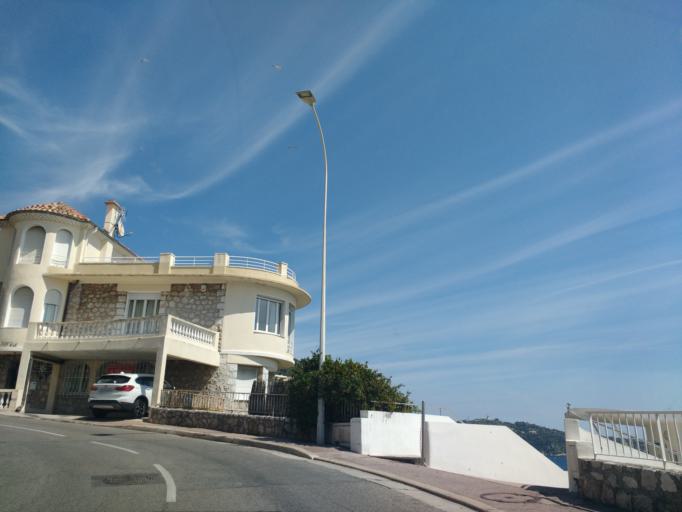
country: FR
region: Provence-Alpes-Cote d'Azur
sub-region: Departement des Alpes-Maritimes
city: Villefranche-sur-Mer
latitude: 43.6866
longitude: 7.2955
